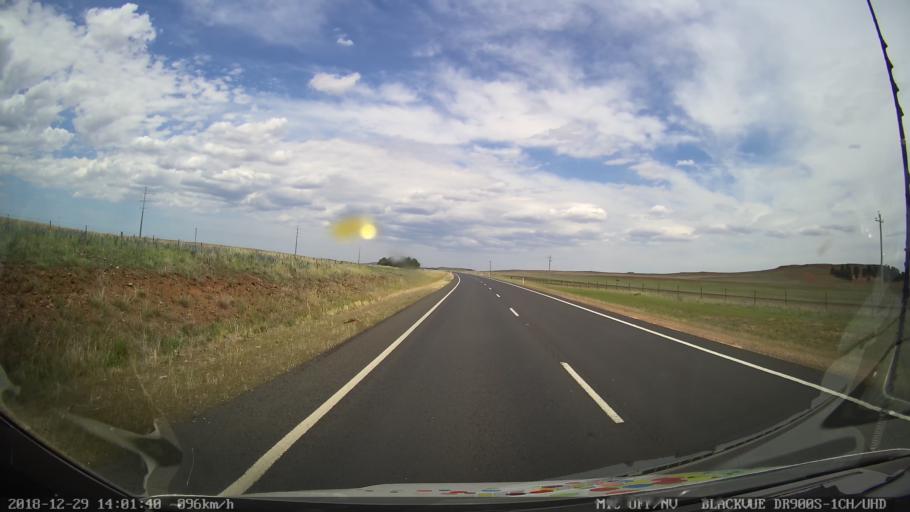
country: AU
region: New South Wales
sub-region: Cooma-Monaro
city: Cooma
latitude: -36.2786
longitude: 149.1695
